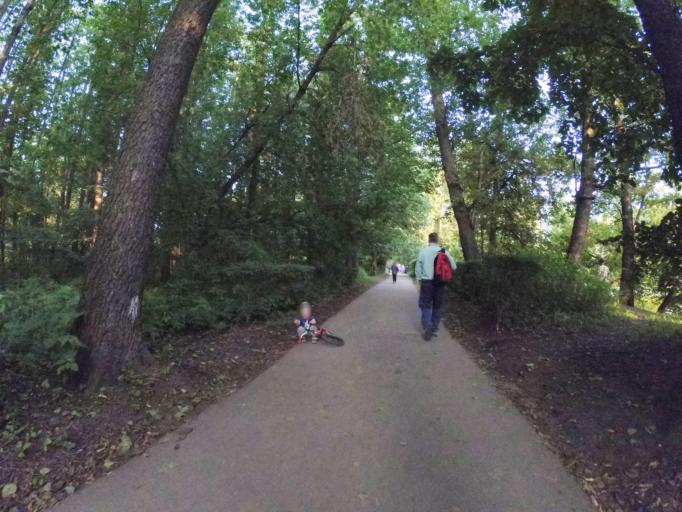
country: RU
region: Moscow
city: Kuz'minki
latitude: 55.6934
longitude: 37.7842
